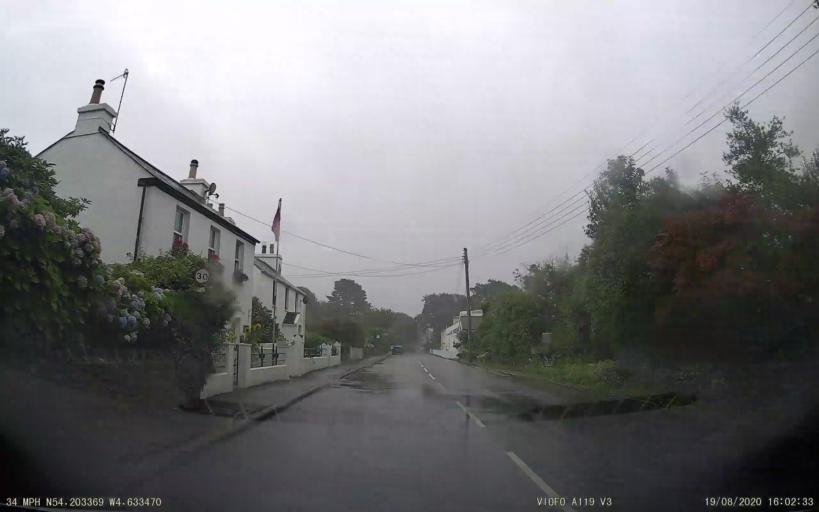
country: IM
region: Castletown
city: Castletown
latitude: 54.2034
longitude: -4.6335
